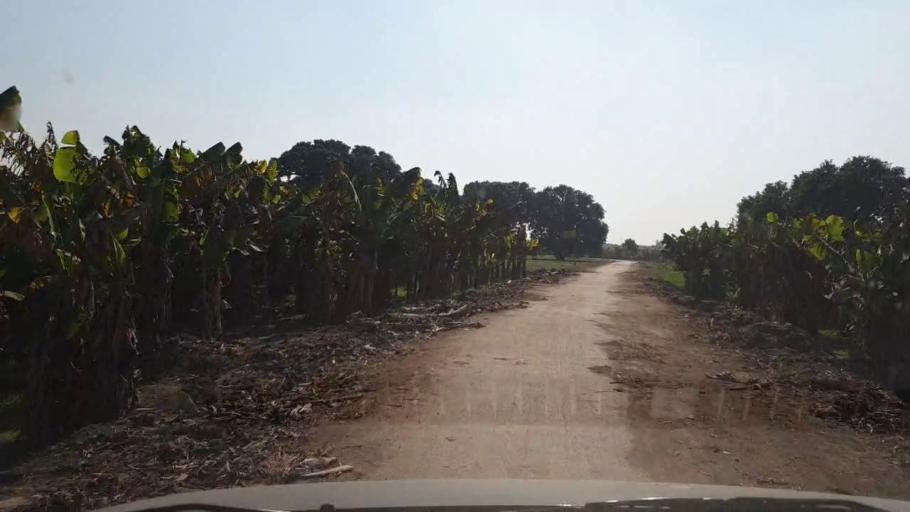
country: PK
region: Sindh
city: Tando Allahyar
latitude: 25.4145
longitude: 68.6341
